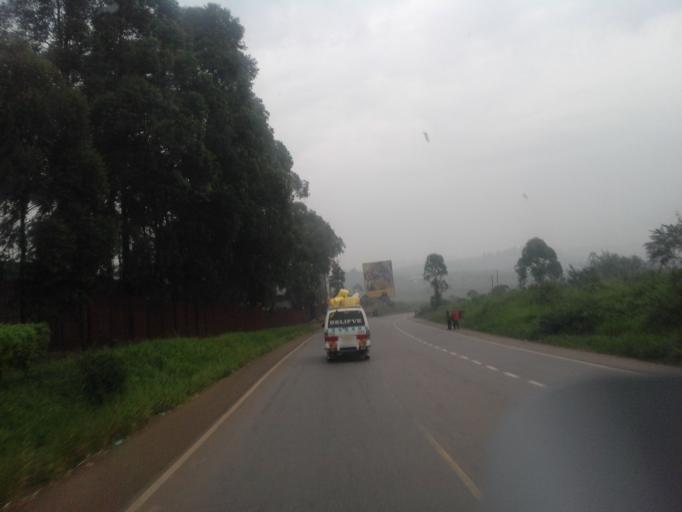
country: UG
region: Central Region
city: Lugazi
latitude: 0.3741
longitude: 32.9071
